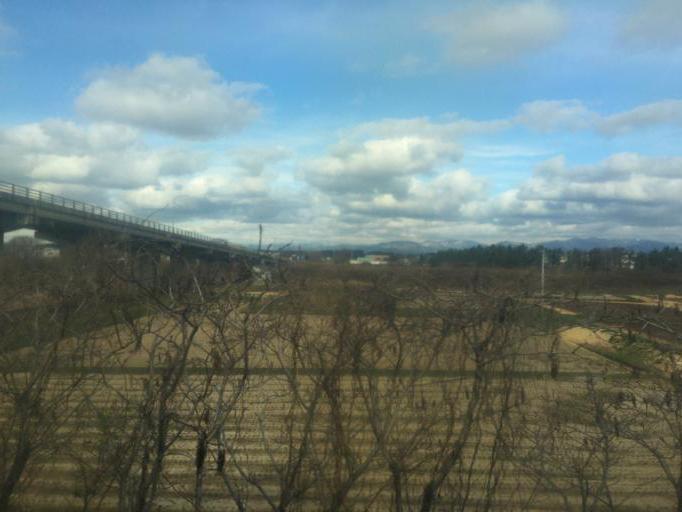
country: JP
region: Akita
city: Noshiromachi
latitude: 40.1948
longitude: 140.0780
